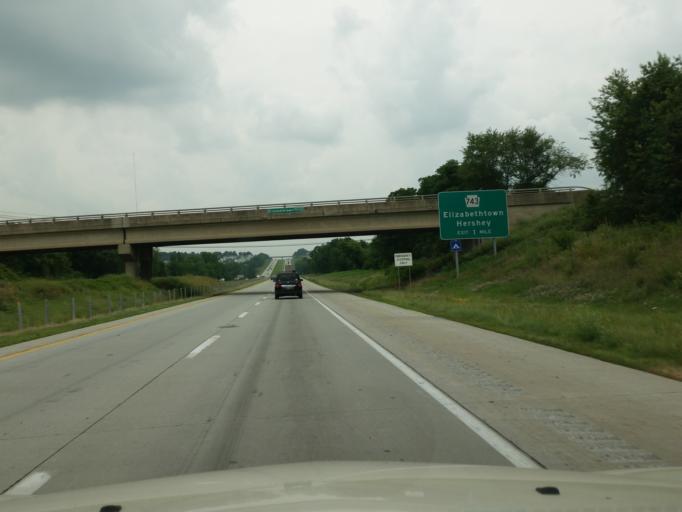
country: US
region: Pennsylvania
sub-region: Lancaster County
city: Elizabethtown
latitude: 40.1626
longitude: -76.5805
